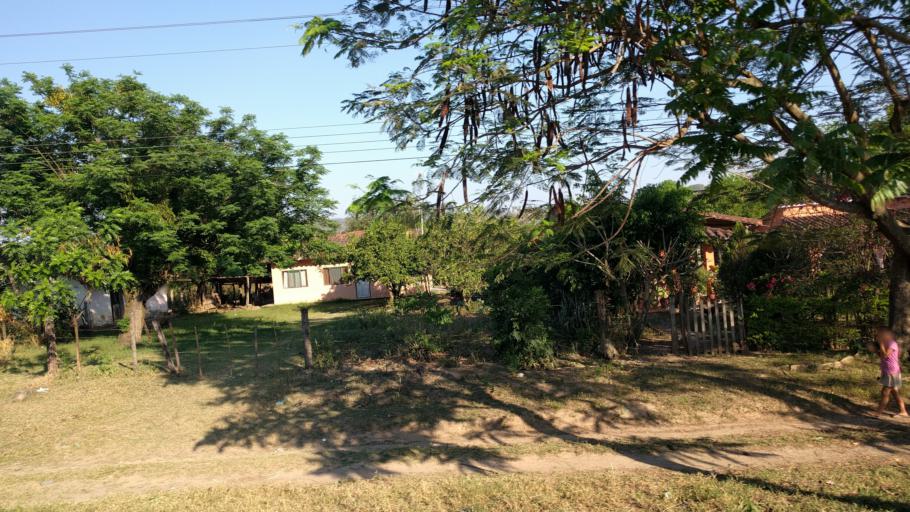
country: BO
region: Santa Cruz
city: Jorochito
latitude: -18.1454
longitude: -63.4829
